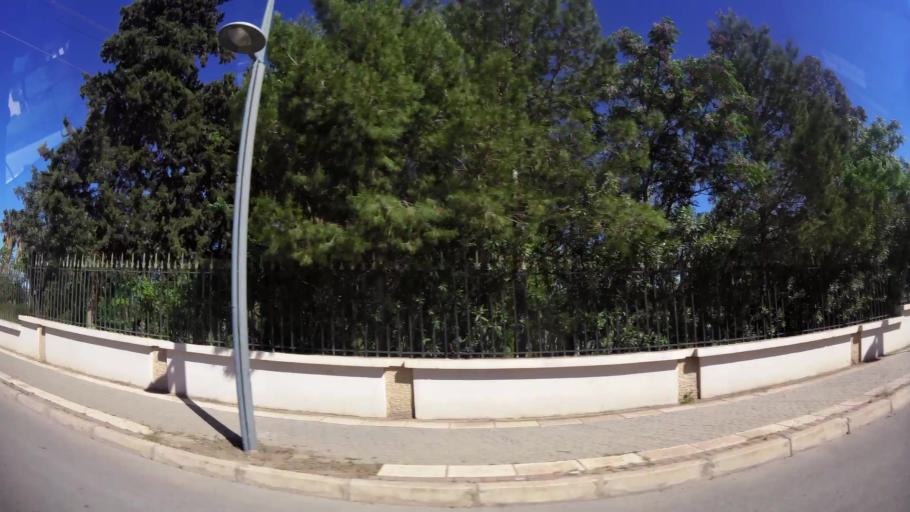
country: MA
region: Oriental
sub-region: Oujda-Angad
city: Oujda
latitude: 34.7207
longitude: -1.9172
